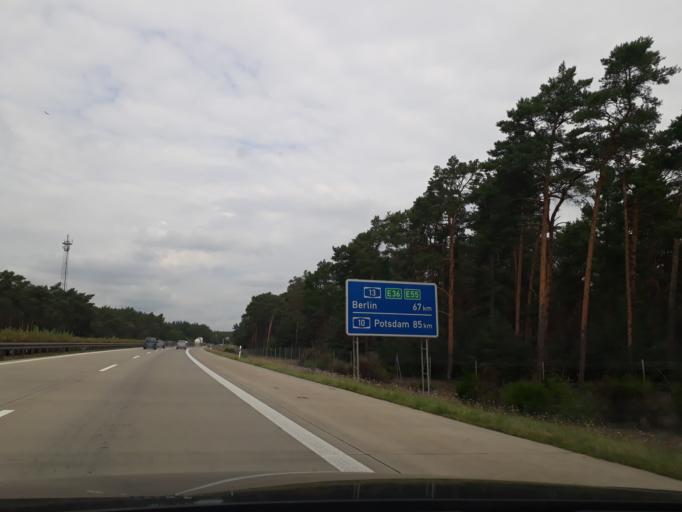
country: DE
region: Brandenburg
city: Kasel-Golzig
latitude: 52.0182
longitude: 13.6909
